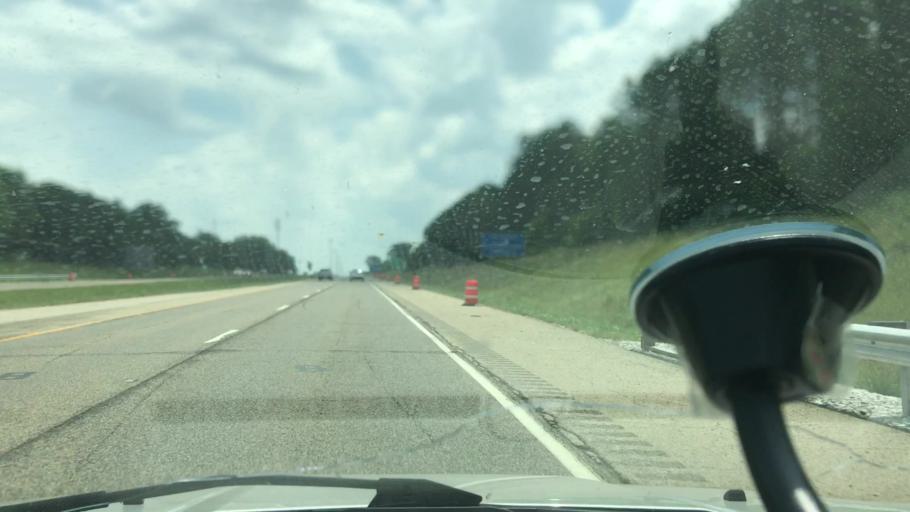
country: US
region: Illinois
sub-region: Peoria County
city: West Peoria
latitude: 40.7392
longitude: -89.6461
